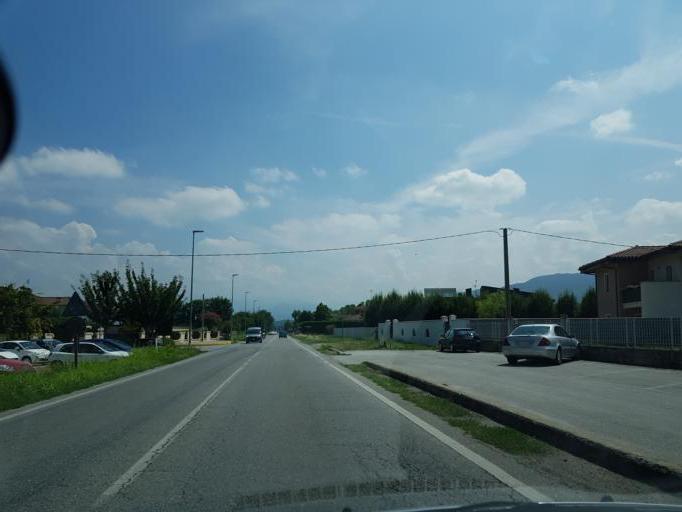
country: IT
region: Piedmont
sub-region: Provincia di Cuneo
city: Caraglio
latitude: 44.4132
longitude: 7.4378
